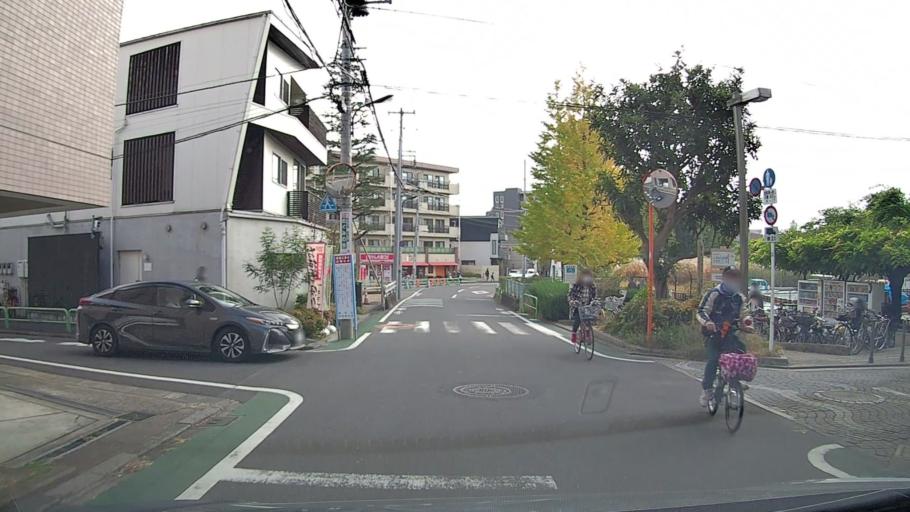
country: JP
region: Saitama
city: Wako
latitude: 35.7408
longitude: 139.6061
